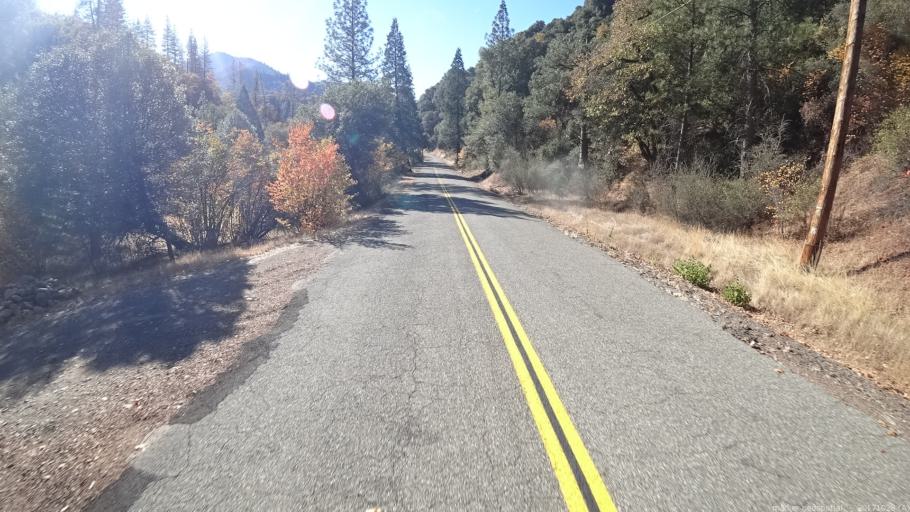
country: US
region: California
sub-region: Shasta County
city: Shasta
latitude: 40.7685
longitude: -122.6100
